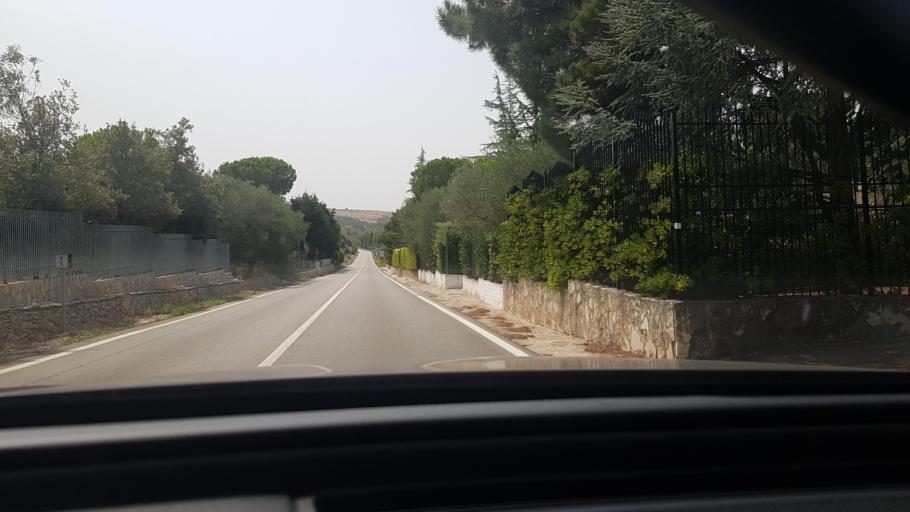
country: IT
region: Apulia
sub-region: Provincia di Barletta - Andria - Trani
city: Andria
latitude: 41.1215
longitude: 16.2856
